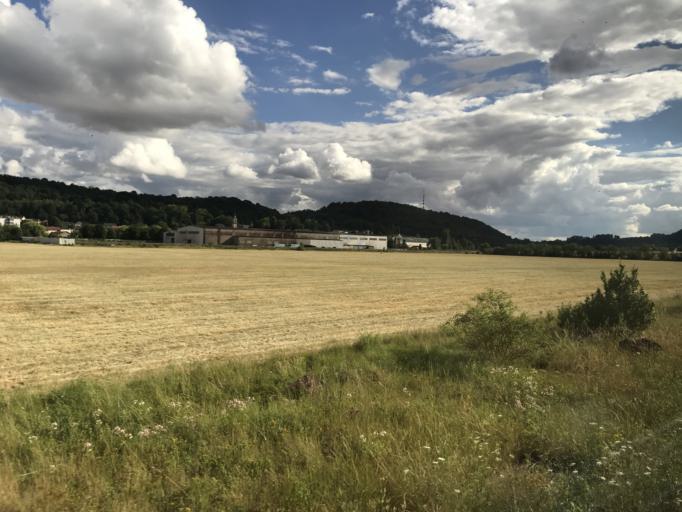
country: FR
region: Lorraine
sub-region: Departement de Meurthe-et-Moselle
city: Longlaville
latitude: 49.5398
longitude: 5.7978
